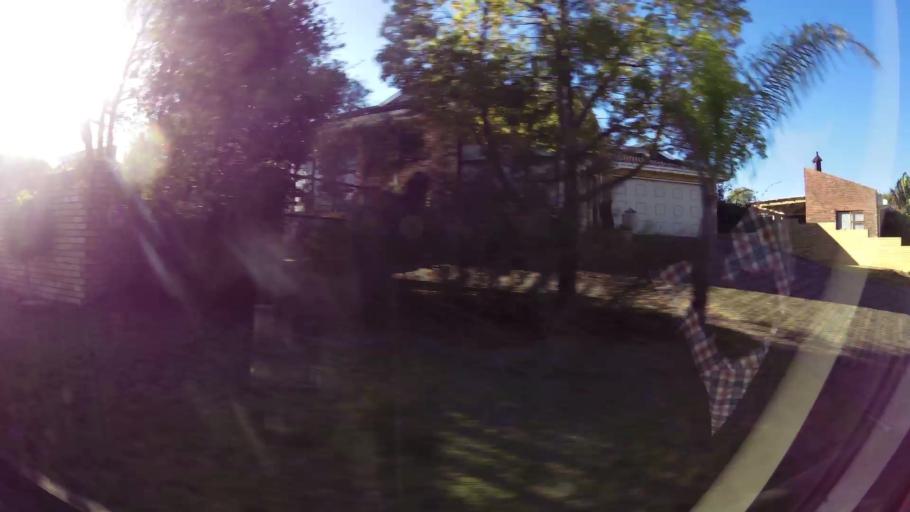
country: ZA
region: Western Cape
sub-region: Eden District Municipality
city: George
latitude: -33.9712
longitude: 22.4376
